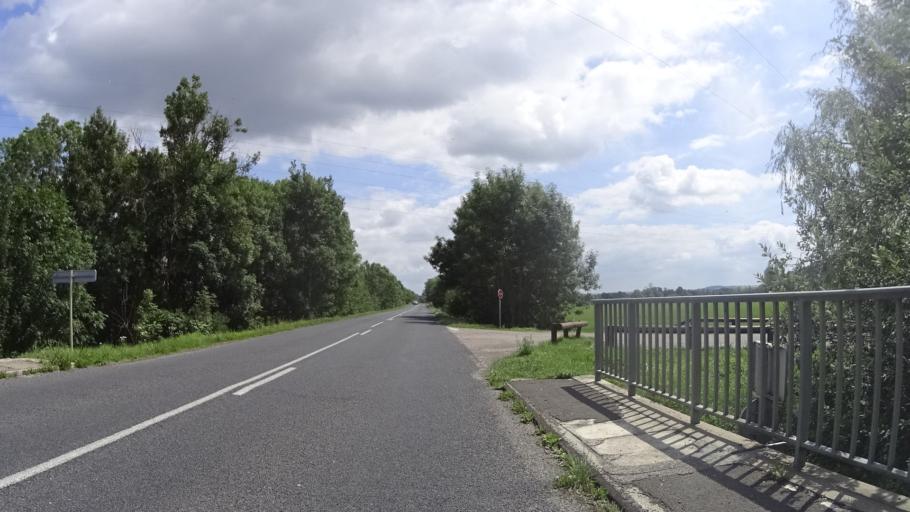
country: FR
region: Lorraine
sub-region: Departement de la Meuse
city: Vignot
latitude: 48.7577
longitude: 5.6080
